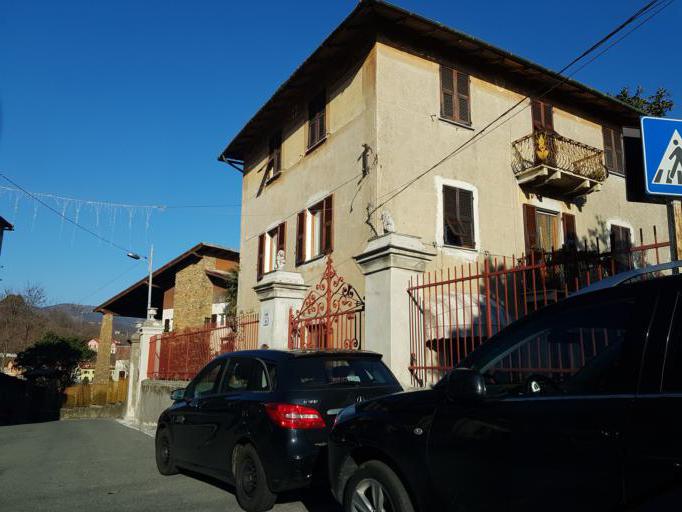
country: IT
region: Liguria
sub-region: Provincia di Genova
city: Campomorone
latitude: 44.5033
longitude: 8.8736
